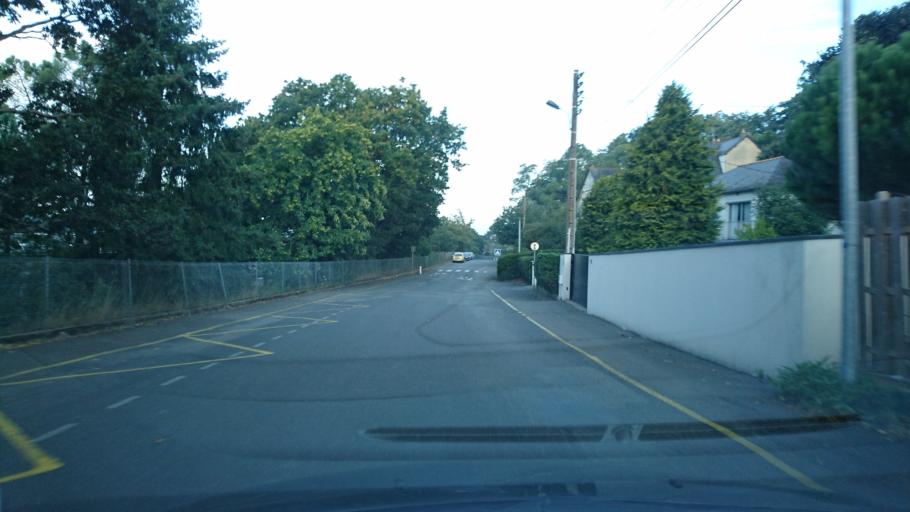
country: FR
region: Brittany
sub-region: Departement d'Ille-et-Vilaine
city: Redon
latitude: 47.6561
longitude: -2.0930
